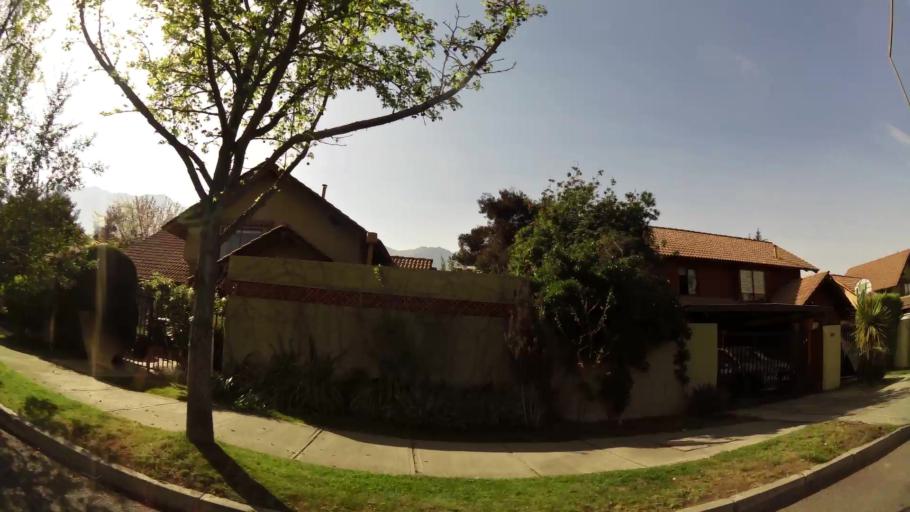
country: CL
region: Santiago Metropolitan
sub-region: Provincia de Santiago
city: Villa Presidente Frei, Nunoa, Santiago, Chile
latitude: -33.4883
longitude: -70.5429
